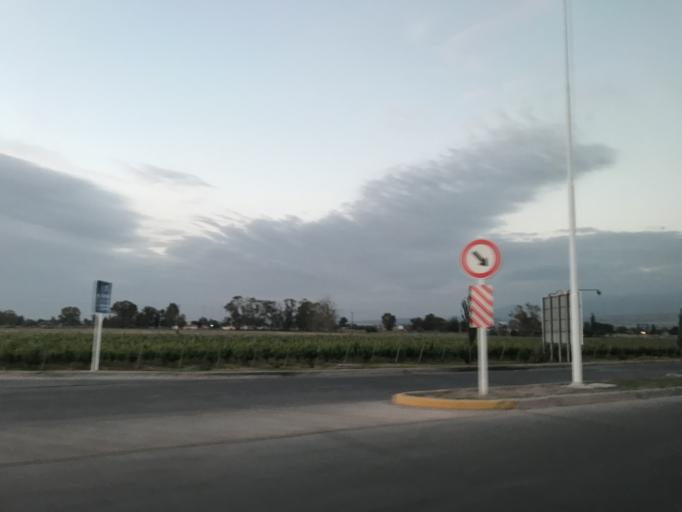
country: AR
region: Mendoza
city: Las Heras
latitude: -32.8278
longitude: -68.8007
